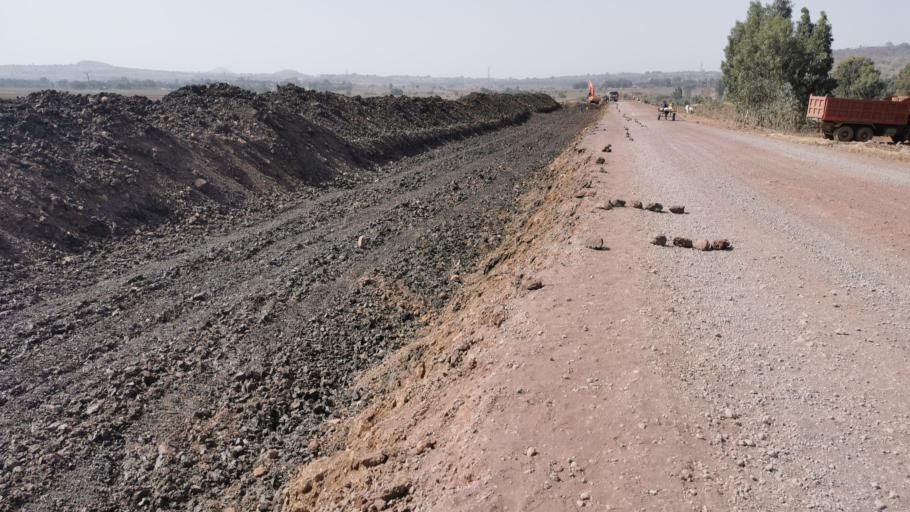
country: ET
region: Amhara
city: Bahir Dar
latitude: 11.8416
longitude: 37.0019
